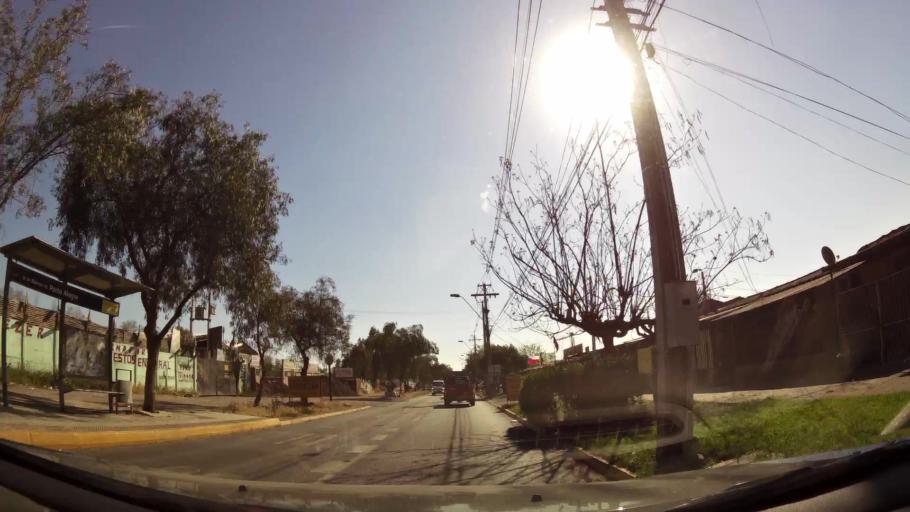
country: CL
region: Santiago Metropolitan
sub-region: Provincia de Santiago
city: La Pintana
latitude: -33.5876
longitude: -70.6398
